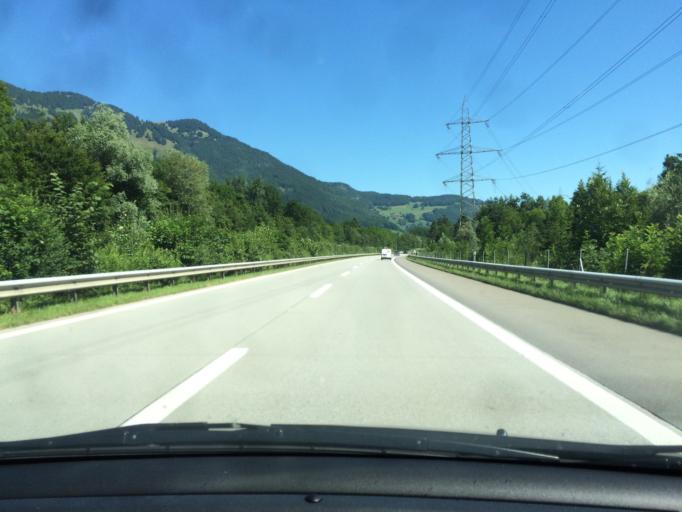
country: CH
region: Saint Gallen
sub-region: Wahlkreis Werdenberg
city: Sennwald
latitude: 47.2674
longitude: 9.5285
